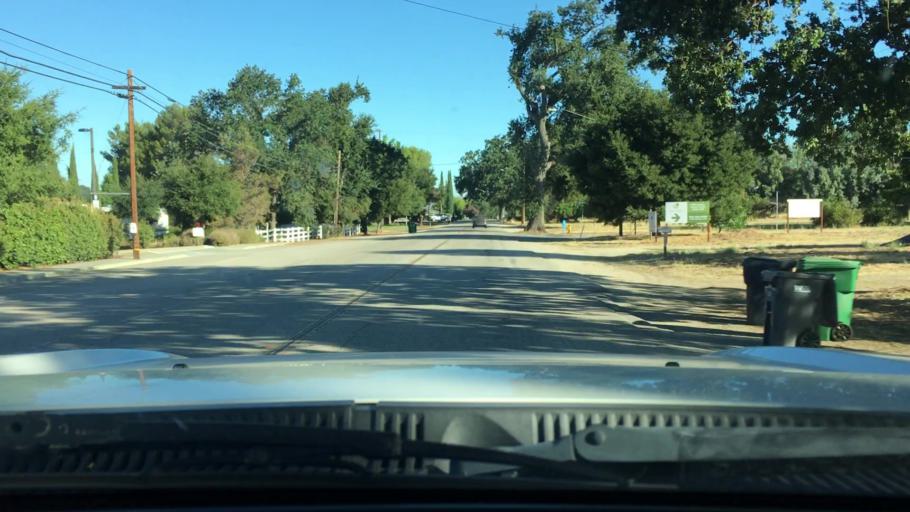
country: US
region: California
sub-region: San Luis Obispo County
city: Templeton
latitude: 35.5173
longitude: -120.7006
